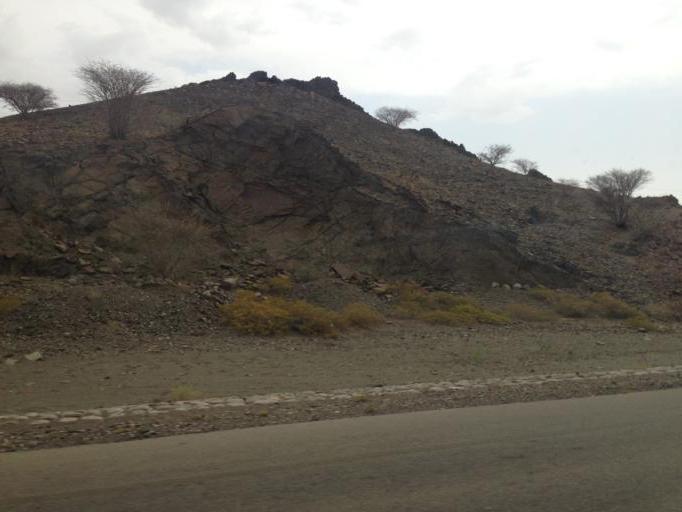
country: OM
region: Ash Sharqiyah
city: Badiyah
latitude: 22.5566
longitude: 59.0086
